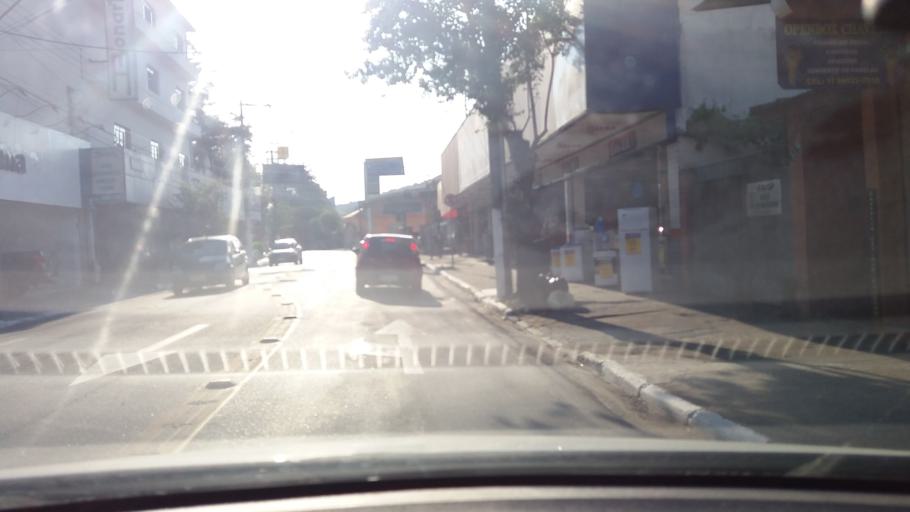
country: BR
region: Sao Paulo
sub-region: Mairipora
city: Mairipora
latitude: -23.3184
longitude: -46.5874
